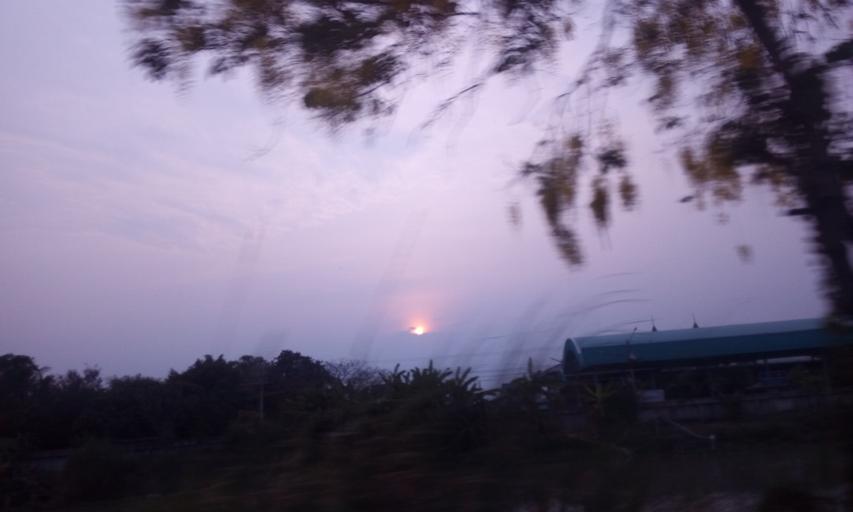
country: TH
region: Pathum Thani
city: Ban Lam Luk Ka
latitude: 13.9956
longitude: 100.8950
